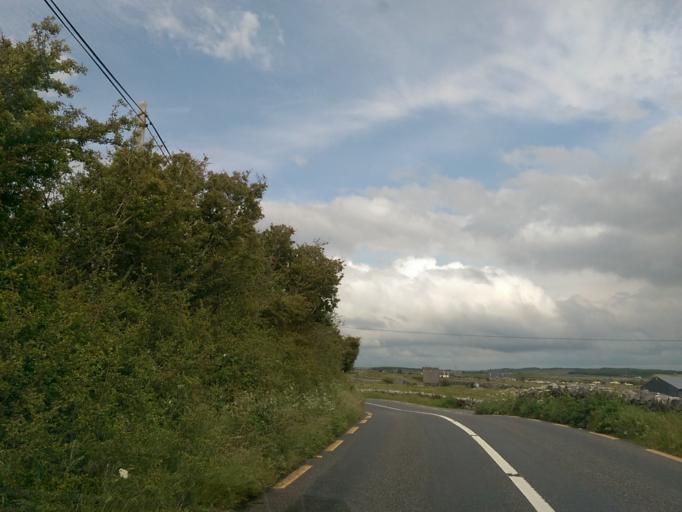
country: IE
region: Connaught
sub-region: County Galway
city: Bearna
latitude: 53.0401
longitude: -9.2739
